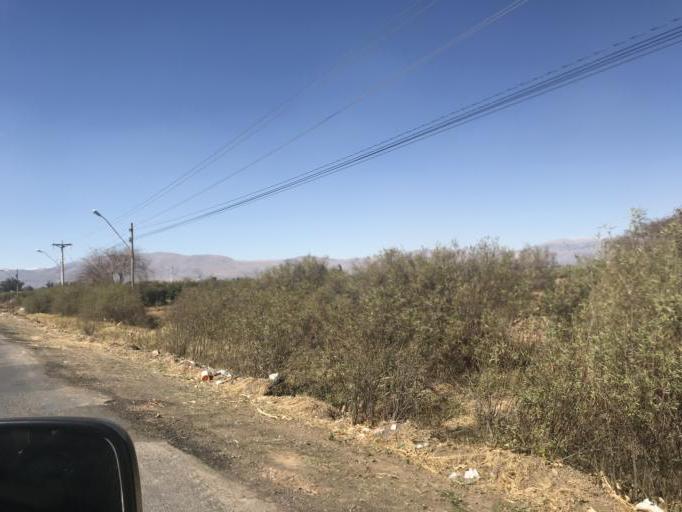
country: BO
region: Cochabamba
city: Cliza
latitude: -17.5707
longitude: -65.8965
